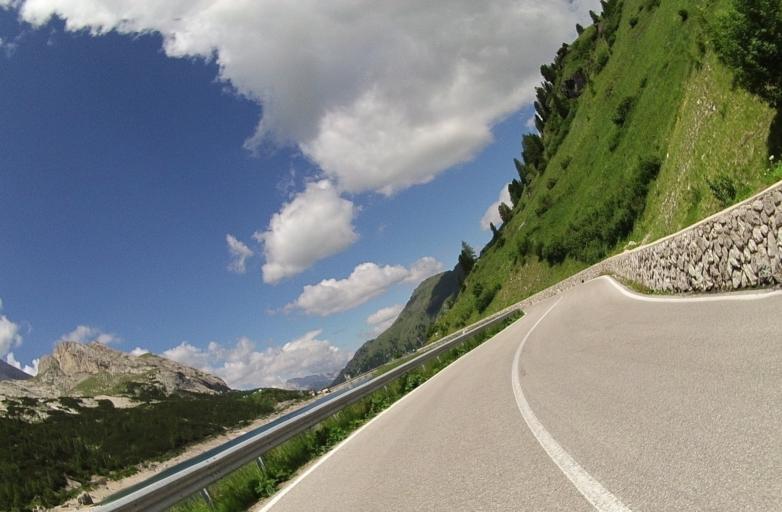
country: IT
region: Veneto
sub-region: Provincia di Belluno
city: Livinallongo del Col di Lana
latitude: 46.4570
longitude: 11.8799
